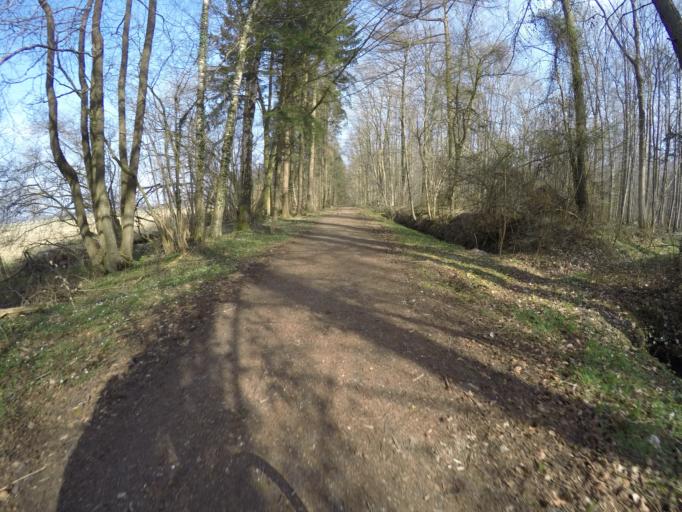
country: DE
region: Schleswig-Holstein
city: Borstel-Hohenraden
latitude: 53.7243
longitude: 9.8096
